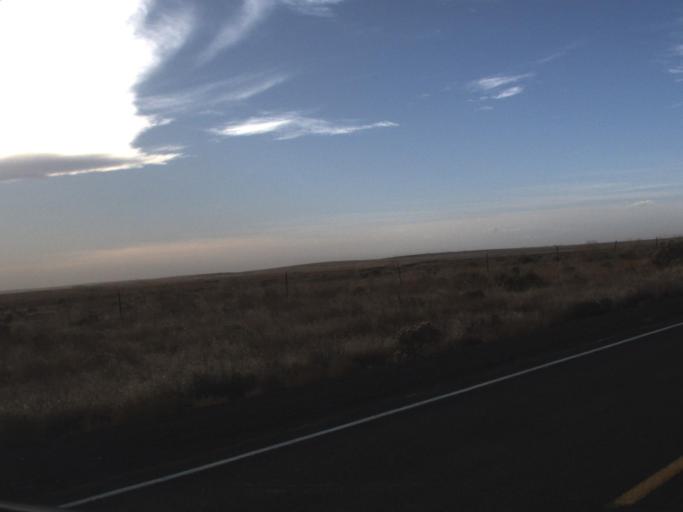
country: US
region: Washington
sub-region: Grant County
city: Warden
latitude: 47.3500
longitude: -118.9344
